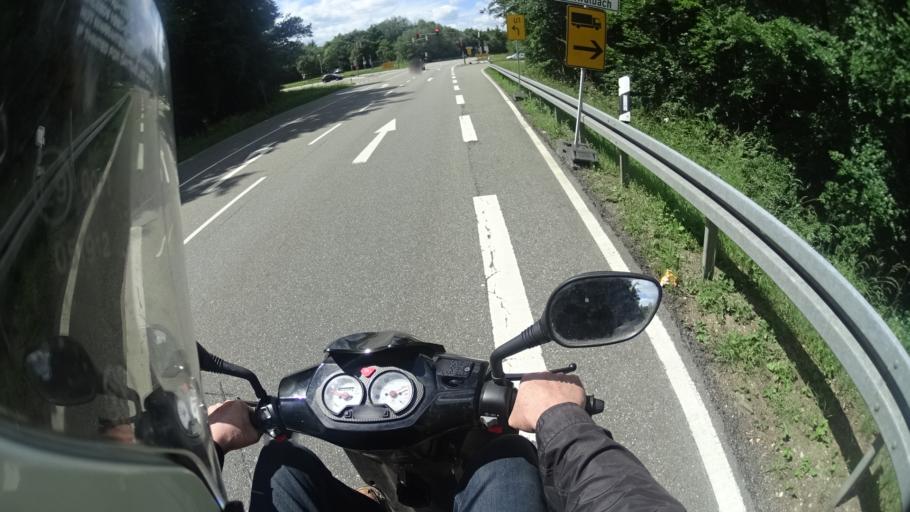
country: DE
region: Hesse
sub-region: Regierungsbezirk Darmstadt
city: Bad Schwalbach
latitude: 50.1267
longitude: 8.0514
